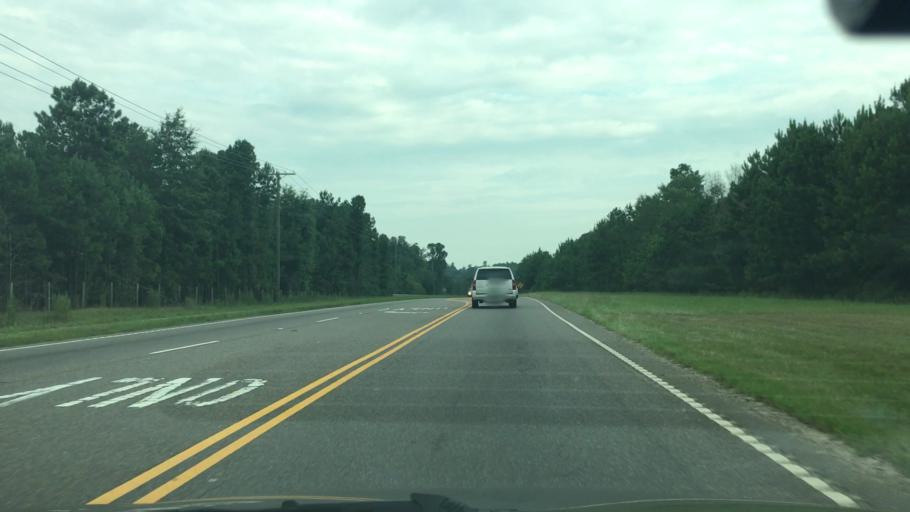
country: US
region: South Carolina
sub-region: Aiken County
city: Aiken
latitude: 33.5648
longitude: -81.6872
